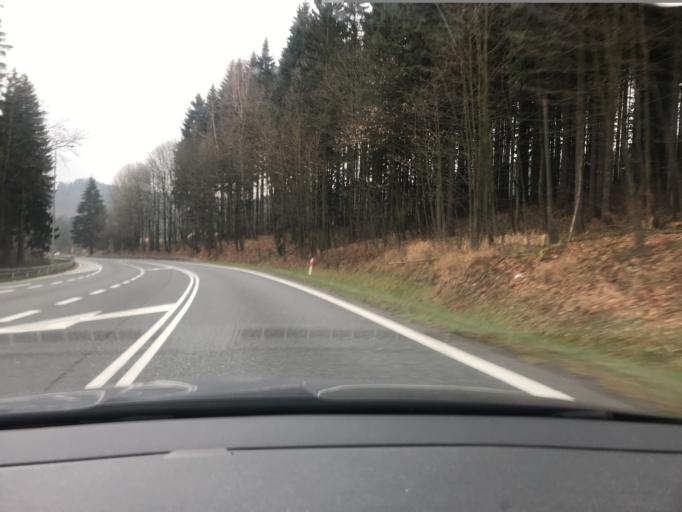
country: PL
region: Lower Silesian Voivodeship
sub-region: Powiat klodzki
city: Duszniki-Zdroj
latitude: 50.3958
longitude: 16.3550
